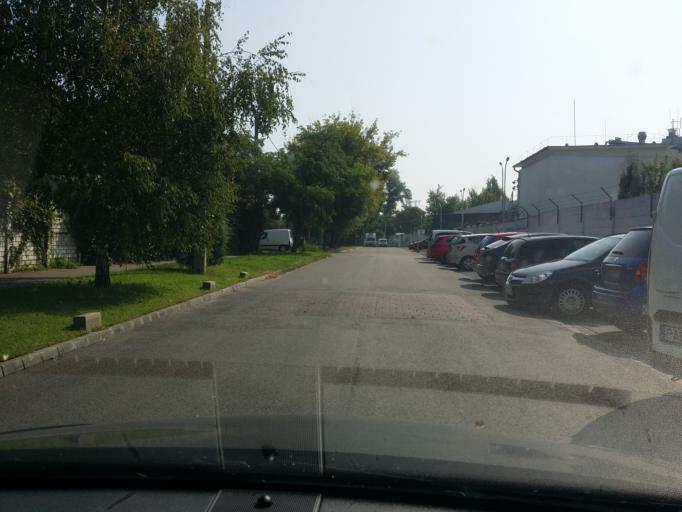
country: HU
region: Budapest
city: Budapest XVI. keruelet
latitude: 47.5000
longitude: 19.1554
